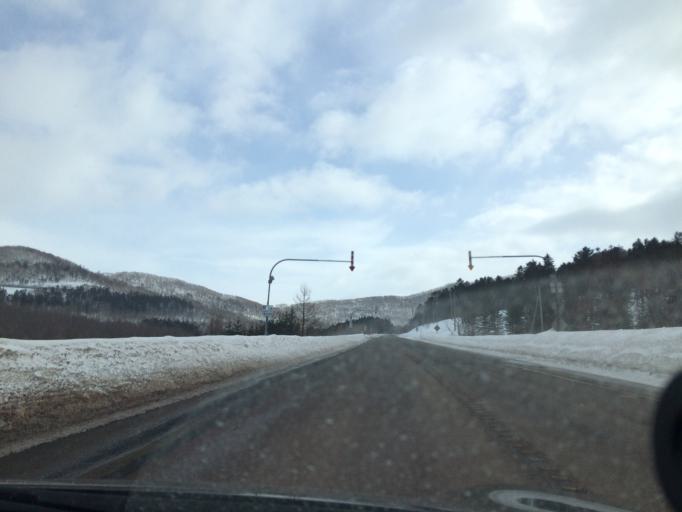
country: JP
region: Hokkaido
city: Shimo-furano
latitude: 43.1372
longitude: 142.7538
